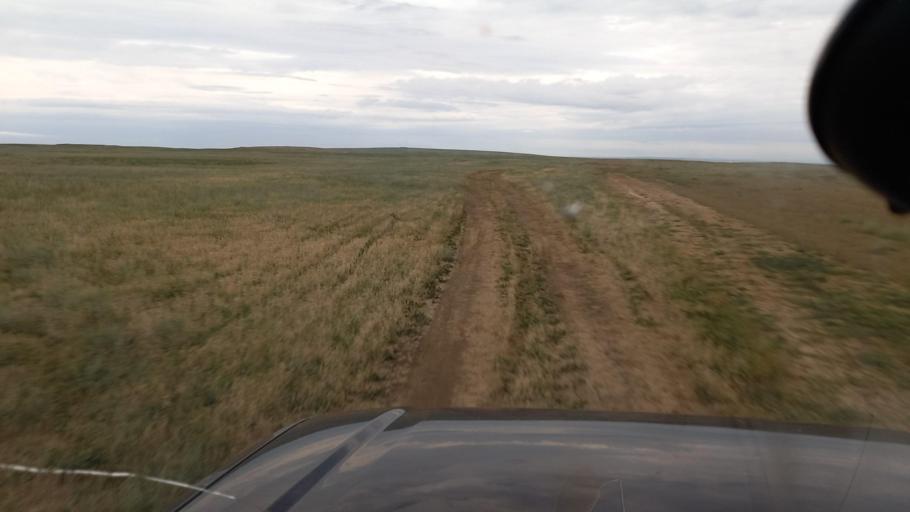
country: RU
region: Krasnodarskiy
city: Taman'
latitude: 45.2014
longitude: 36.7836
